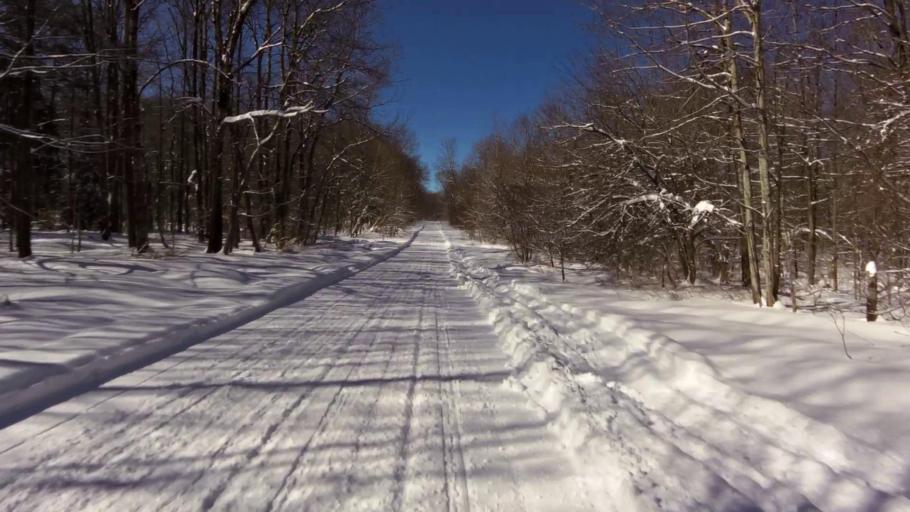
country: US
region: New York
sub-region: Chautauqua County
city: Mayville
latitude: 42.2343
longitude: -79.3784
